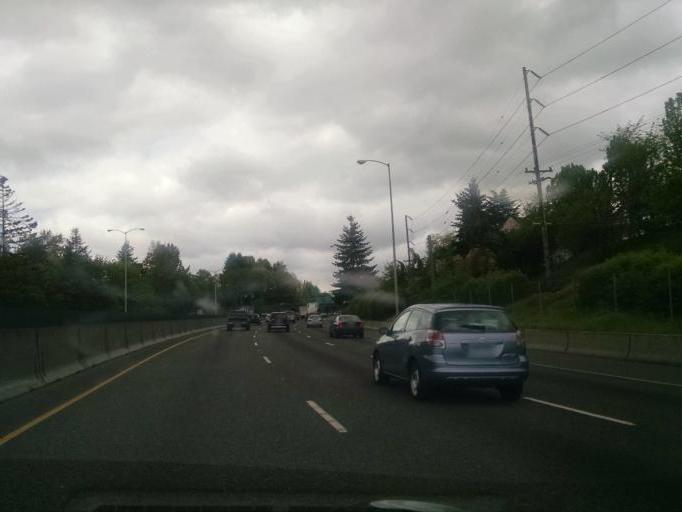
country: US
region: Oregon
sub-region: Clackamas County
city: Lake Oswego
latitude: 45.4681
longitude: -122.6916
